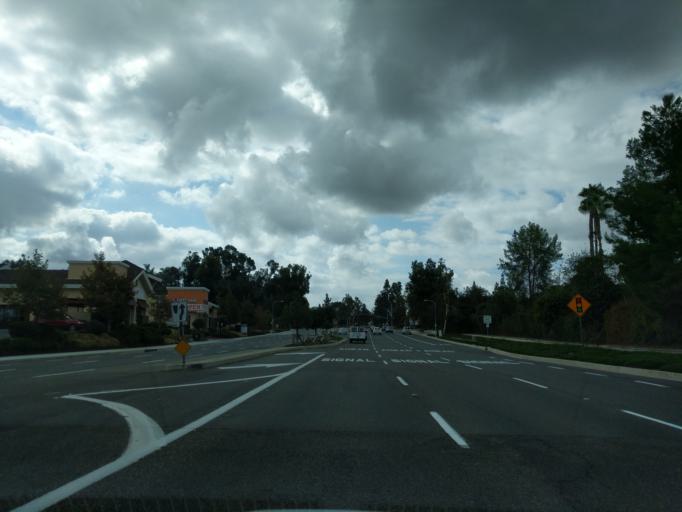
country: US
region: California
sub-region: Orange County
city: Aliso Viejo
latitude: 33.5778
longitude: -117.7029
